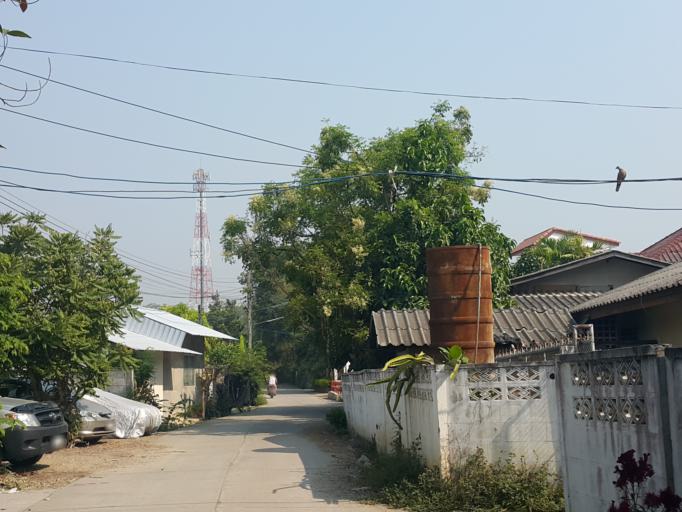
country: TH
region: Chiang Mai
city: Saraphi
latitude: 18.7263
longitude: 99.0219
